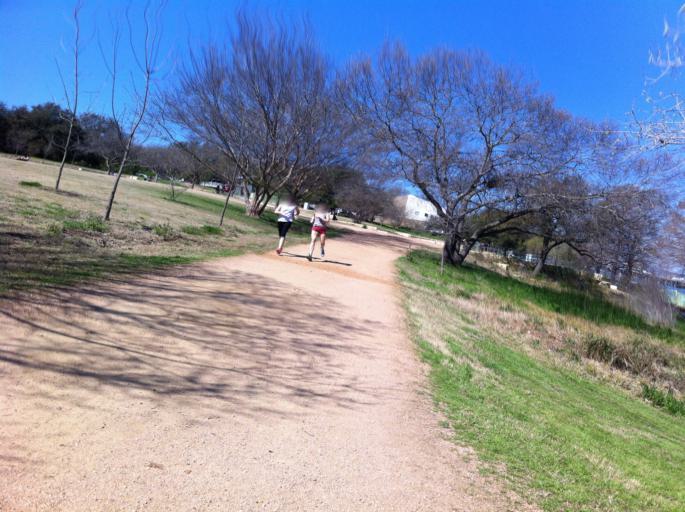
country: US
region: Texas
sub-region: Travis County
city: Austin
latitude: 30.2448
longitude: -97.7240
